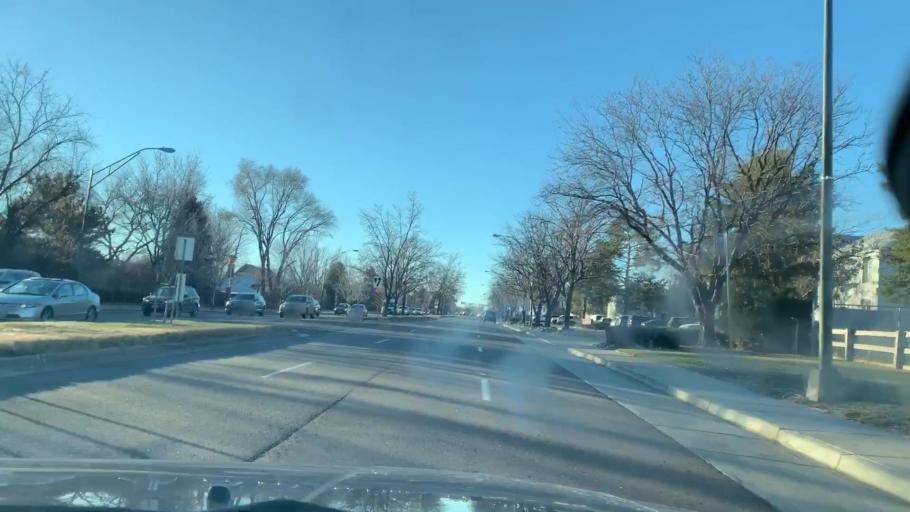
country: US
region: Colorado
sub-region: Arapahoe County
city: Cherry Hills Village
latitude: 39.6564
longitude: -104.9130
